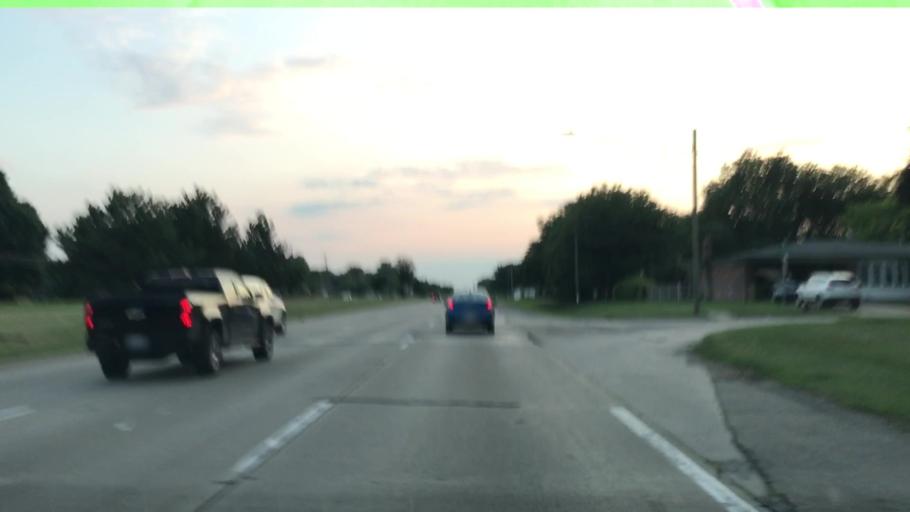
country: US
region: Michigan
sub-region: Macomb County
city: Sterling Heights
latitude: 42.5665
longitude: -83.0142
